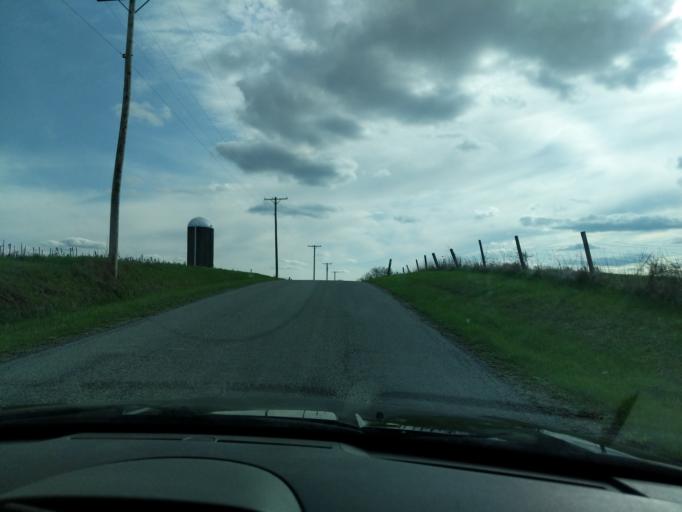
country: US
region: Ohio
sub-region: Champaign County
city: Urbana
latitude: 40.1351
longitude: -83.6541
